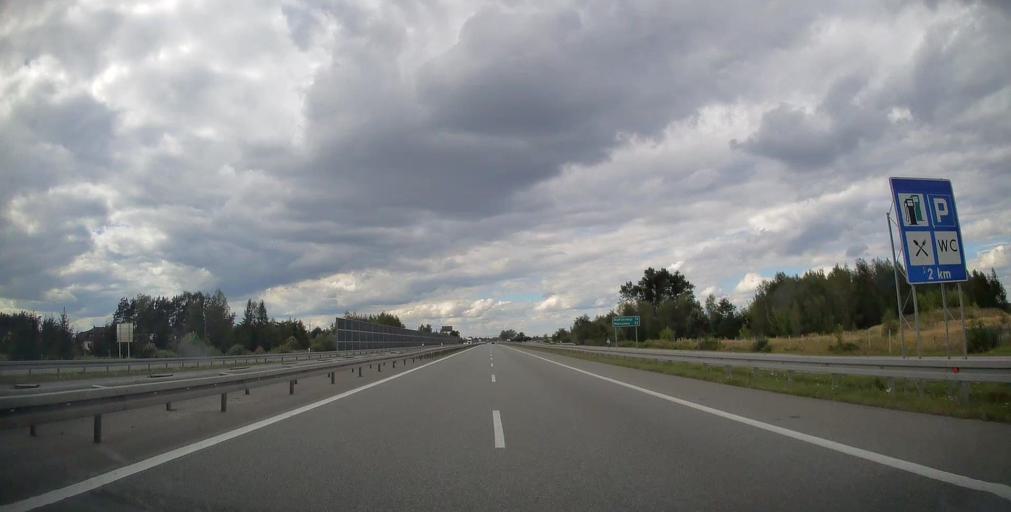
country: PL
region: Masovian Voivodeship
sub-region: Powiat bialobrzeski
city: Stara Blotnica
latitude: 51.5529
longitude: 21.0392
